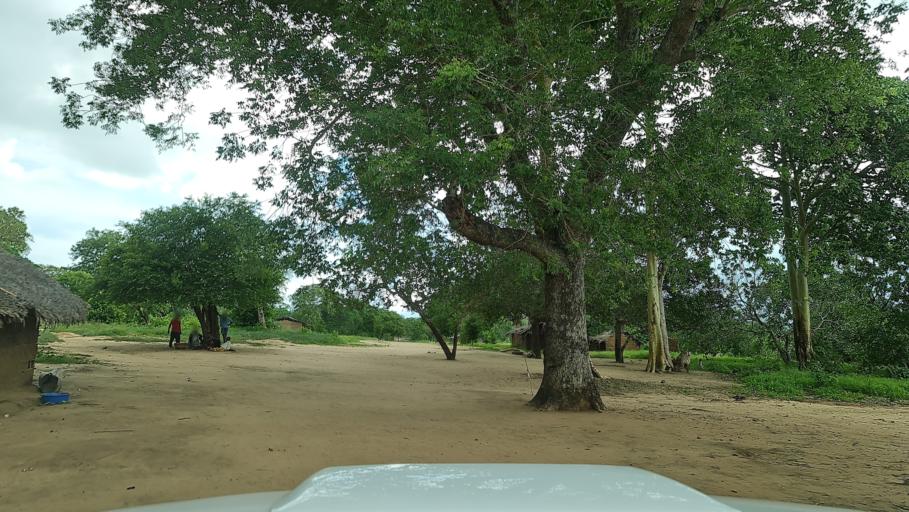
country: MZ
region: Nampula
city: Ilha de Mocambique
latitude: -15.4983
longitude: 40.1597
